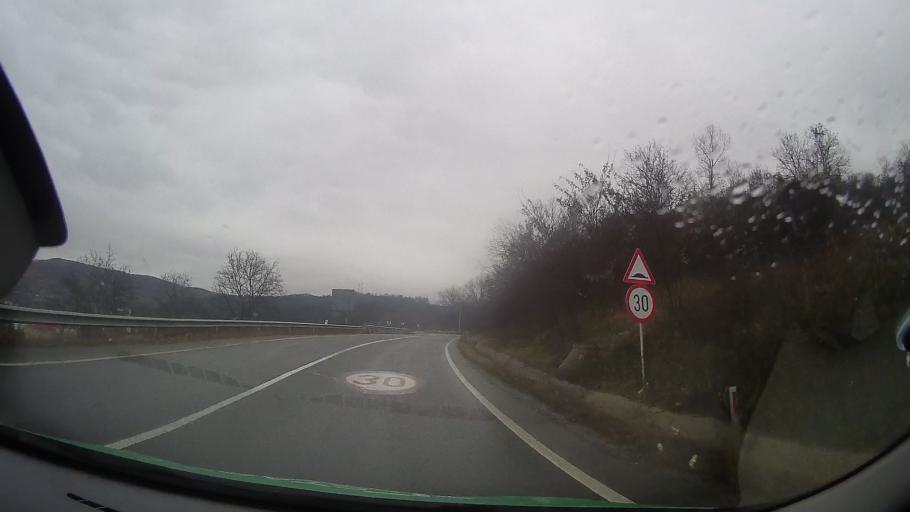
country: RO
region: Bistrita-Nasaud
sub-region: Comuna Teaca
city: Teaca
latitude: 46.9089
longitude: 24.4979
